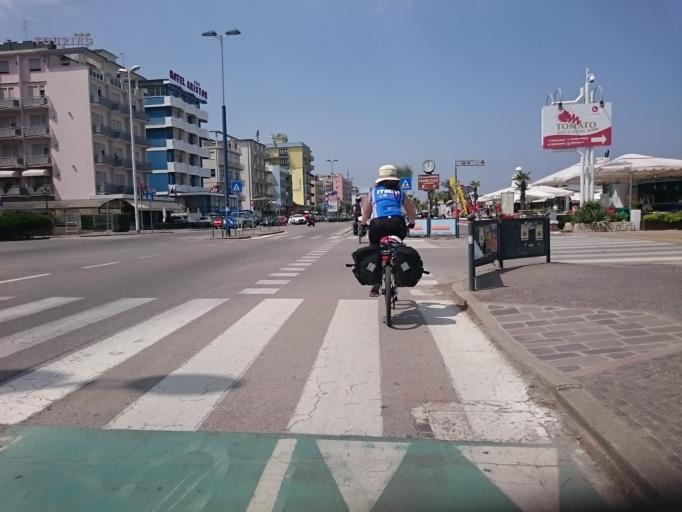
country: IT
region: Veneto
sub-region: Provincia di Venezia
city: Chioggia
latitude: 45.2125
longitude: 12.2953
